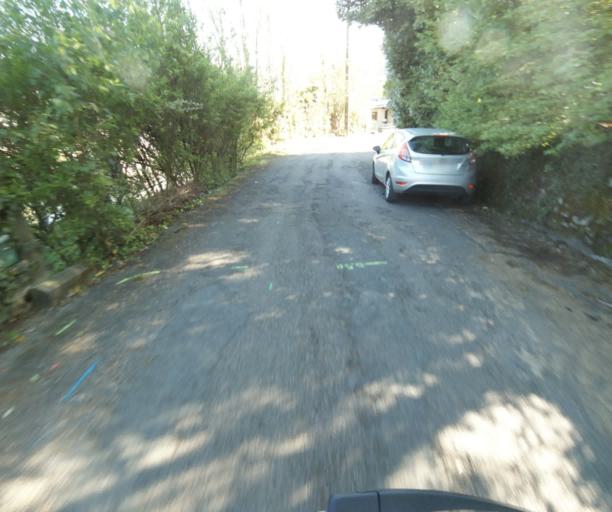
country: FR
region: Limousin
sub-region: Departement de la Correze
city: Tulle
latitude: 45.2619
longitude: 1.7662
